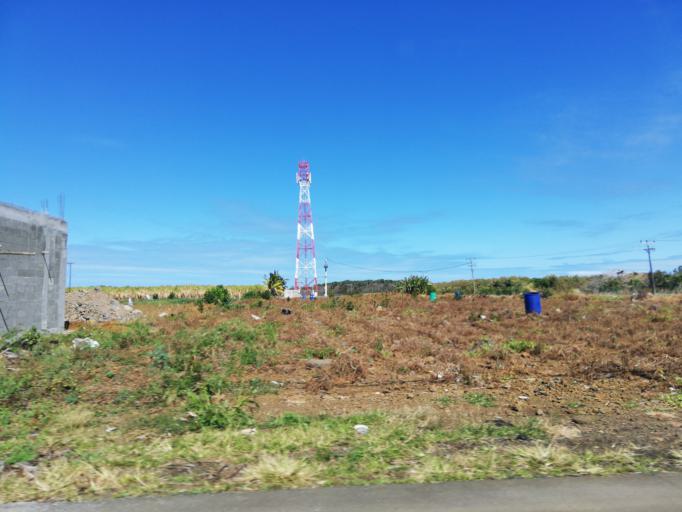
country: MU
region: Grand Port
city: Beau Vallon
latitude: -20.4450
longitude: 57.6915
